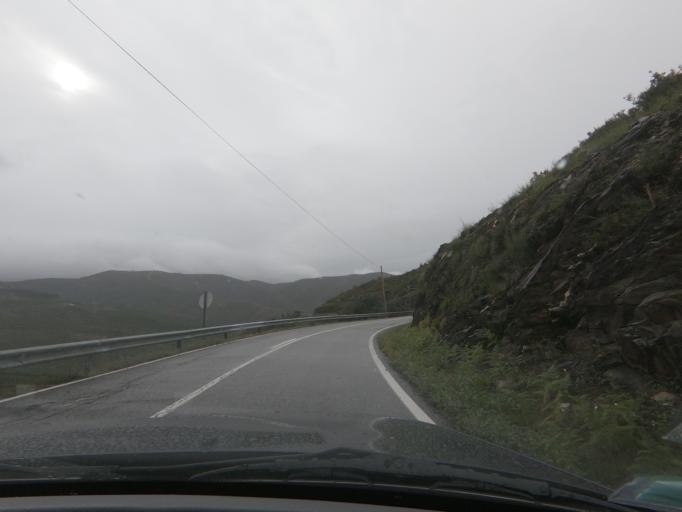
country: PT
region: Vila Real
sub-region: Mondim de Basto
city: Mondim de Basto
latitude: 41.3519
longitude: -7.9076
